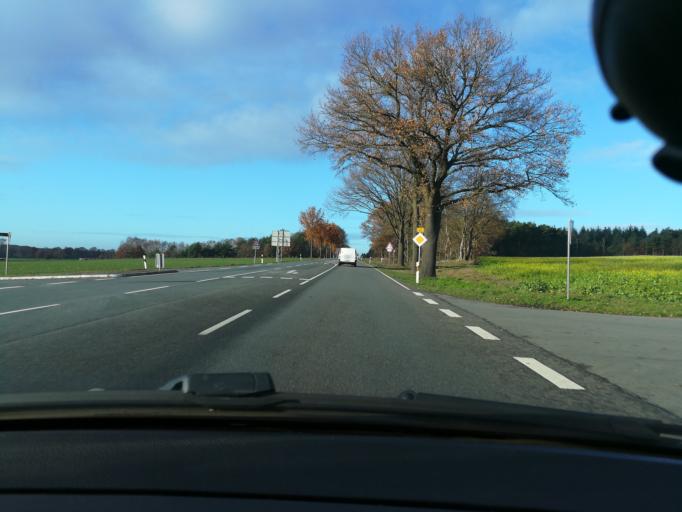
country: DE
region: Lower Saxony
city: Uchte
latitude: 52.5291
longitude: 8.8833
